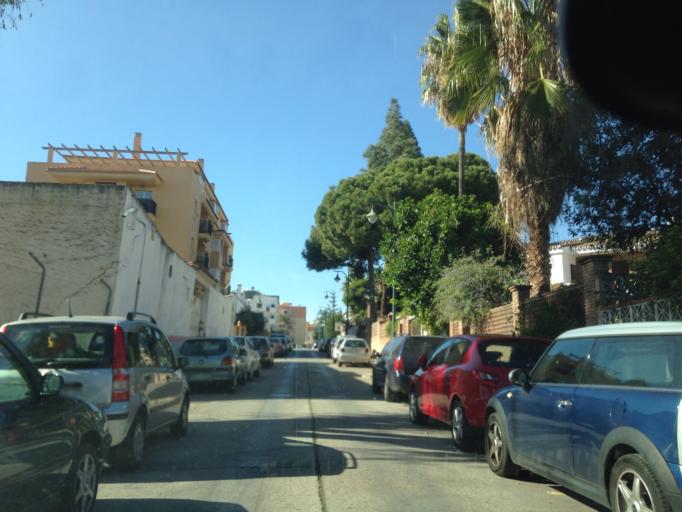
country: ES
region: Andalusia
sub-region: Provincia de Malaga
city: Malaga
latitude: 36.7215
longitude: -4.4508
